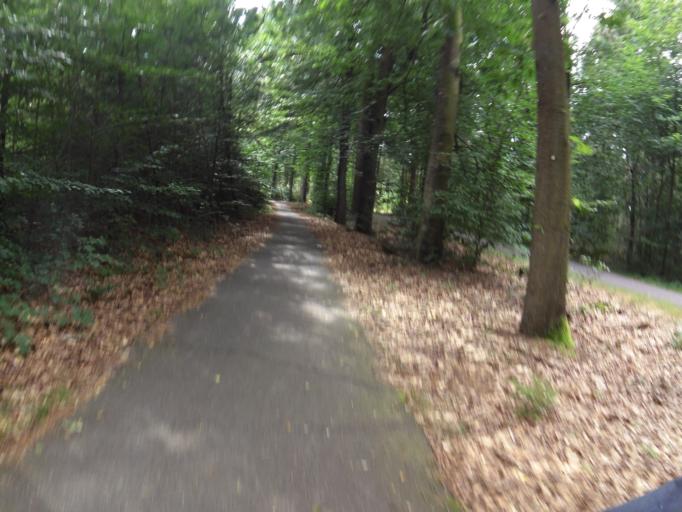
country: NL
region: Drenthe
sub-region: Gemeente Borger-Odoorn
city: Borger
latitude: 52.9727
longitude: 6.7587
